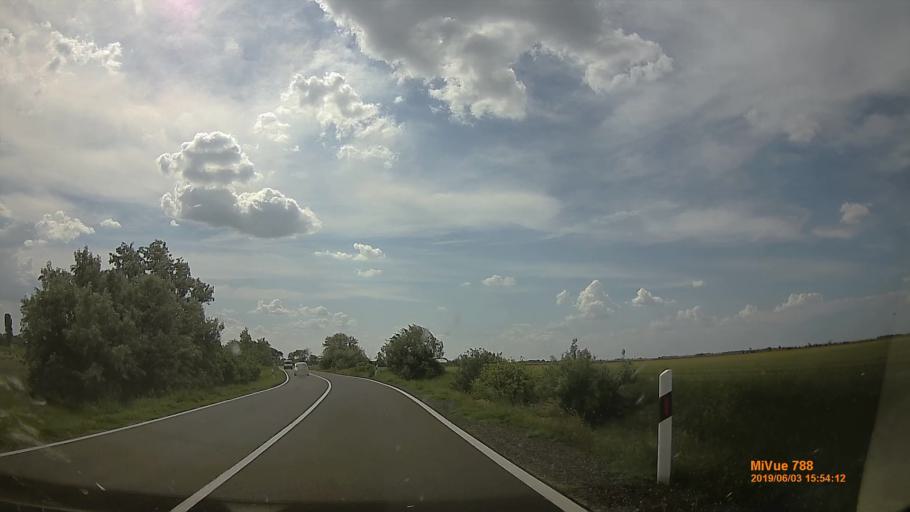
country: HU
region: Bacs-Kiskun
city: Akaszto
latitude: 46.7466
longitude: 19.1332
